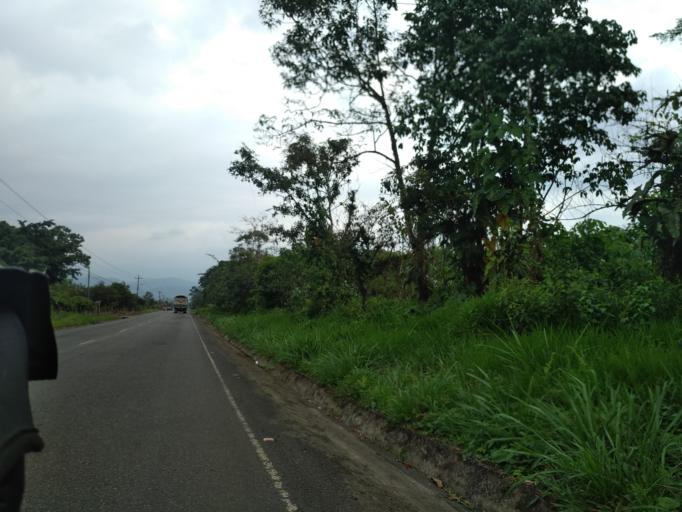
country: EC
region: Cotopaxi
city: La Mana
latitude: -0.8880
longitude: -79.1612
